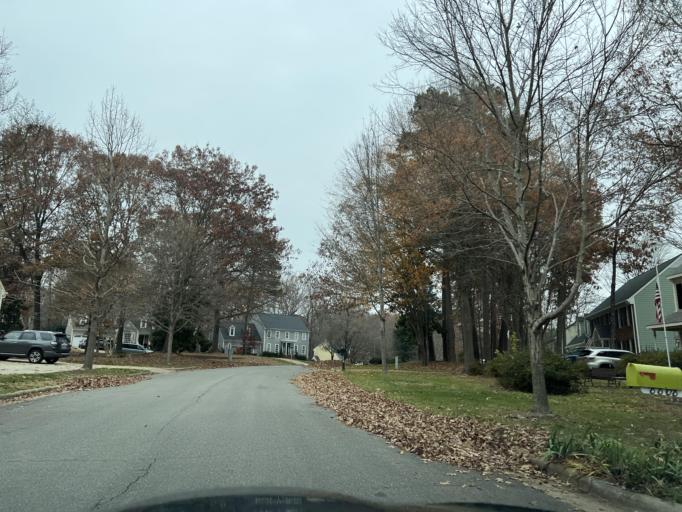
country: US
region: North Carolina
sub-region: Wake County
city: Wake Forest
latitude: 35.8969
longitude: -78.6025
